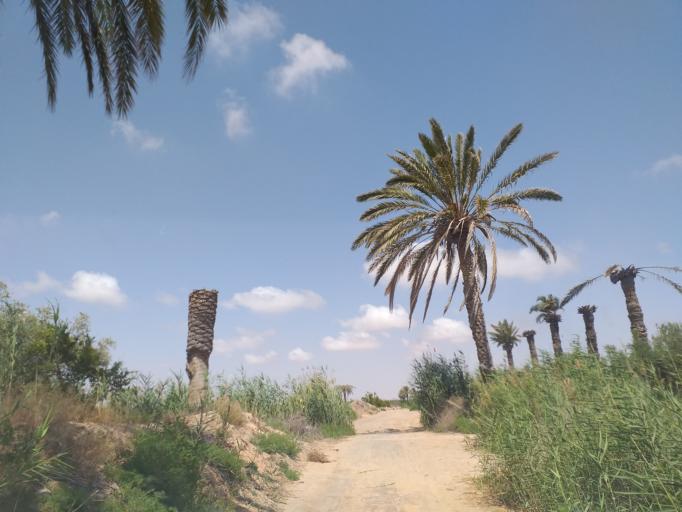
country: TN
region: Qabis
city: Gabes
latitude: 33.9515
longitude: 10.0492
